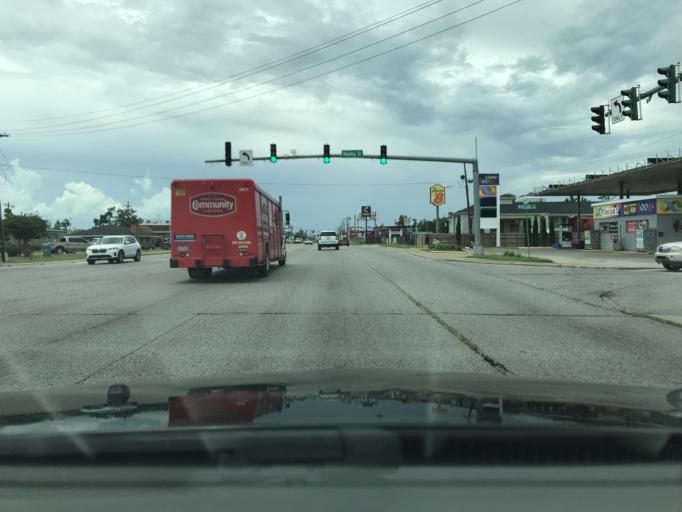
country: US
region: Louisiana
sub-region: Calcasieu Parish
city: Lake Charles
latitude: 30.2493
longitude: -93.1804
